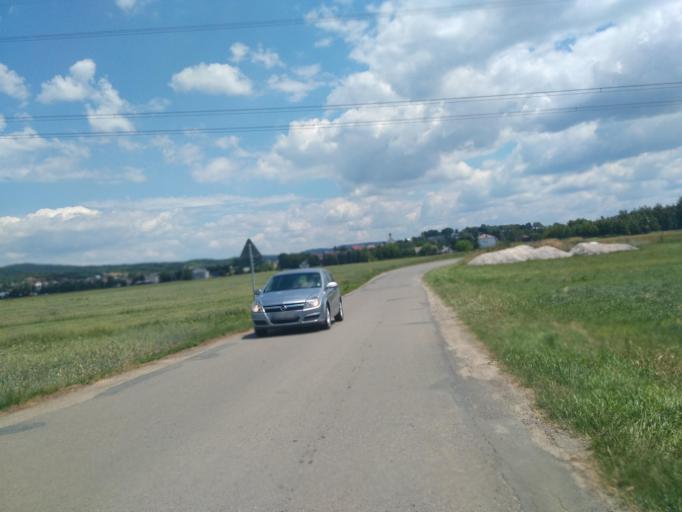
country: PL
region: Subcarpathian Voivodeship
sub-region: Powiat debicki
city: Brzostek
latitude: 49.8769
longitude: 21.3954
